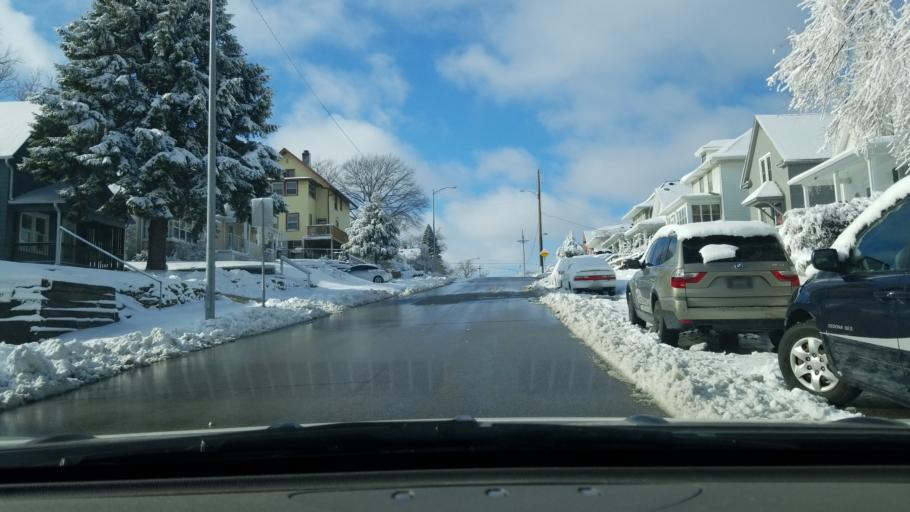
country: US
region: Nebraska
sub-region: Douglas County
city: Omaha
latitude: 41.2198
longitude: -95.9431
